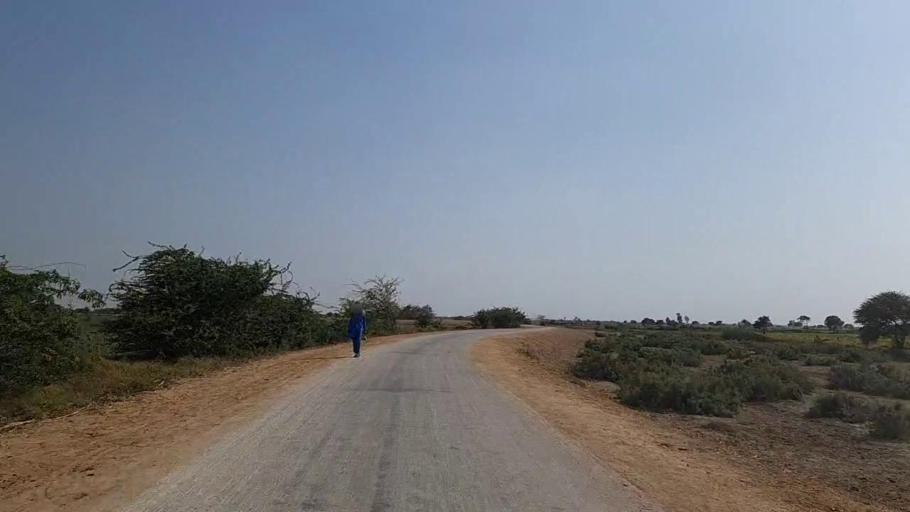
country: PK
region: Sindh
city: Daro Mehar
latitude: 24.7803
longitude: 68.1803
